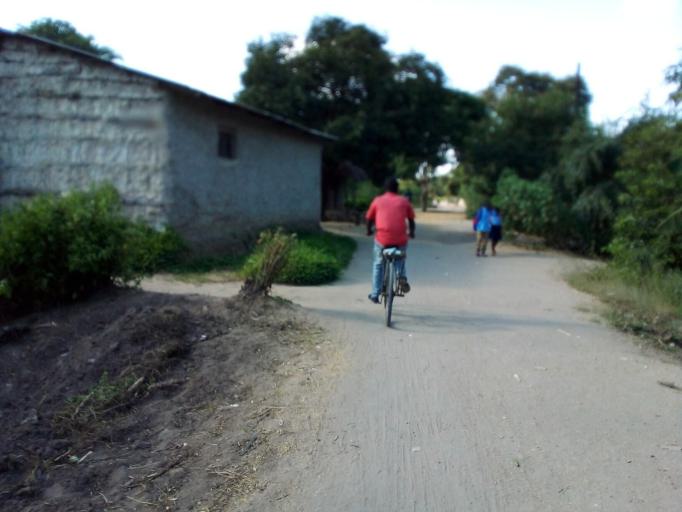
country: MZ
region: Zambezia
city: Quelimane
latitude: -17.6024
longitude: 36.8228
